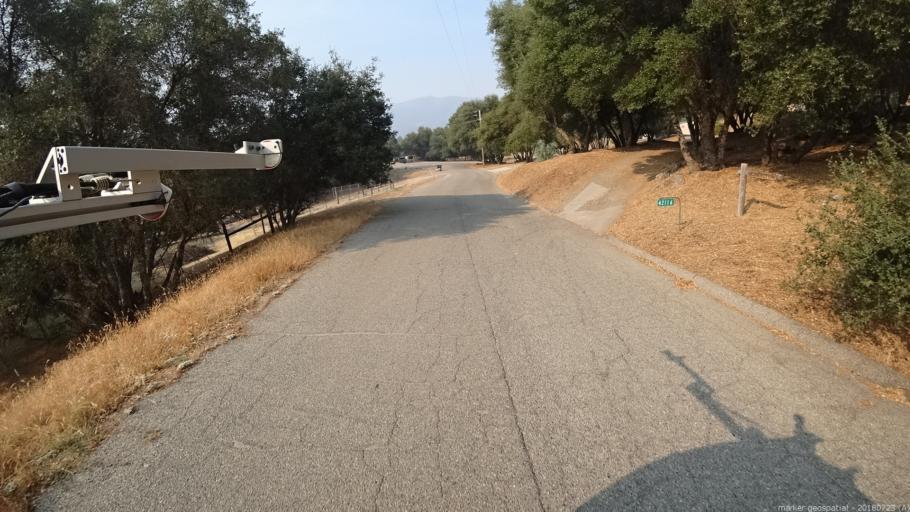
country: US
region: California
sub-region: Madera County
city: Ahwahnee
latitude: 37.3609
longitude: -119.7148
